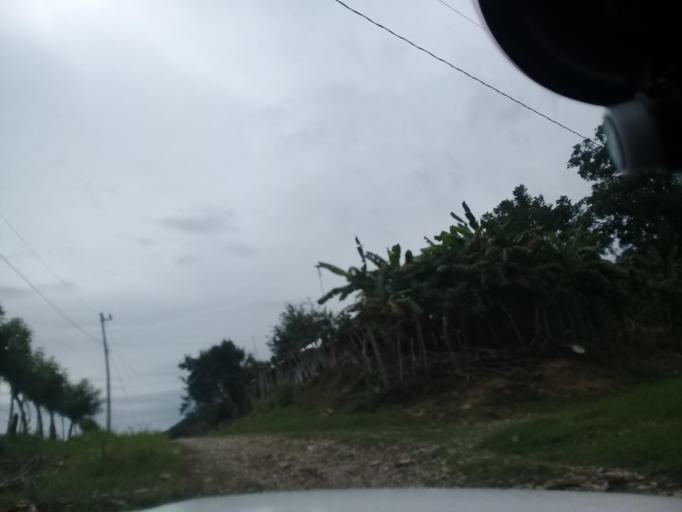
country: MX
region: Veracruz
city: Platon Sanchez
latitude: 21.2185
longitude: -98.3585
